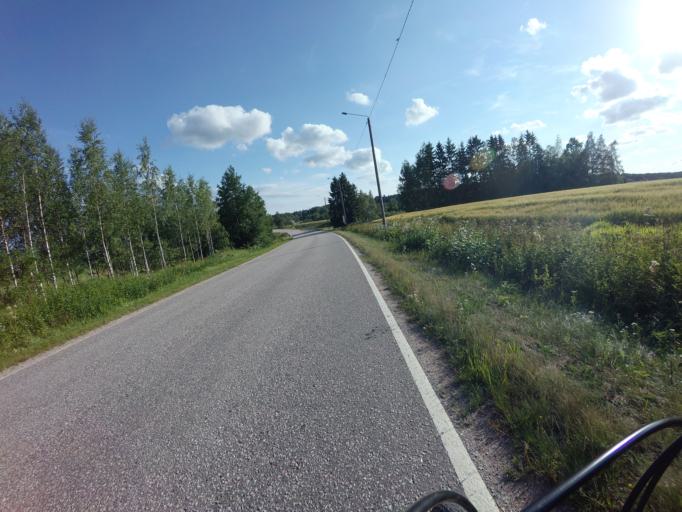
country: FI
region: Varsinais-Suomi
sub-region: Turku
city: Vahto
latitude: 60.5571
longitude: 22.3437
